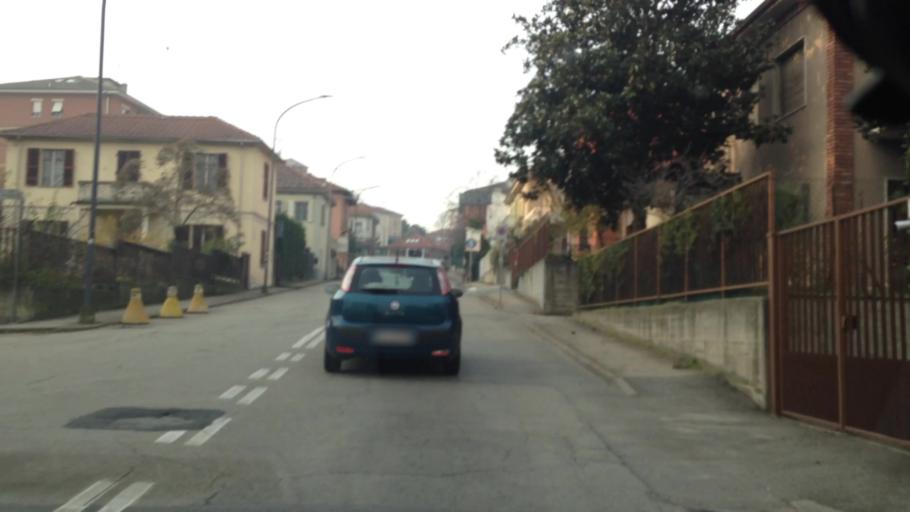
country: IT
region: Piedmont
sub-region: Provincia di Asti
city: Asti
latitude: 44.9052
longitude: 8.2099
